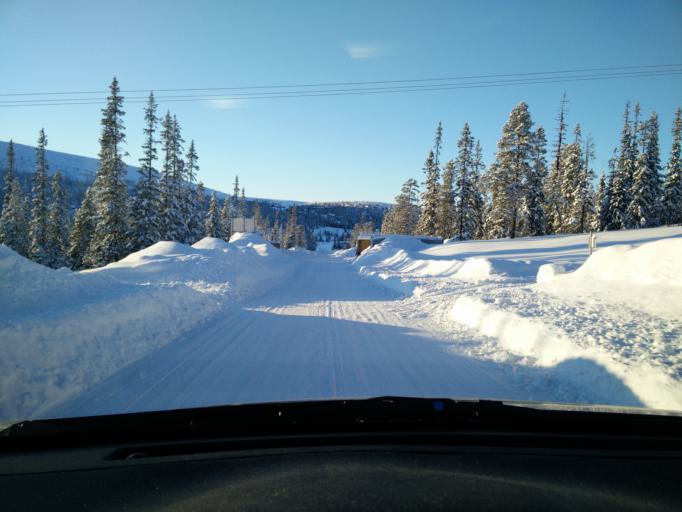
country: SE
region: Jaemtland
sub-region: Bergs Kommun
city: Hoverberg
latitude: 62.4959
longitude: 14.1226
